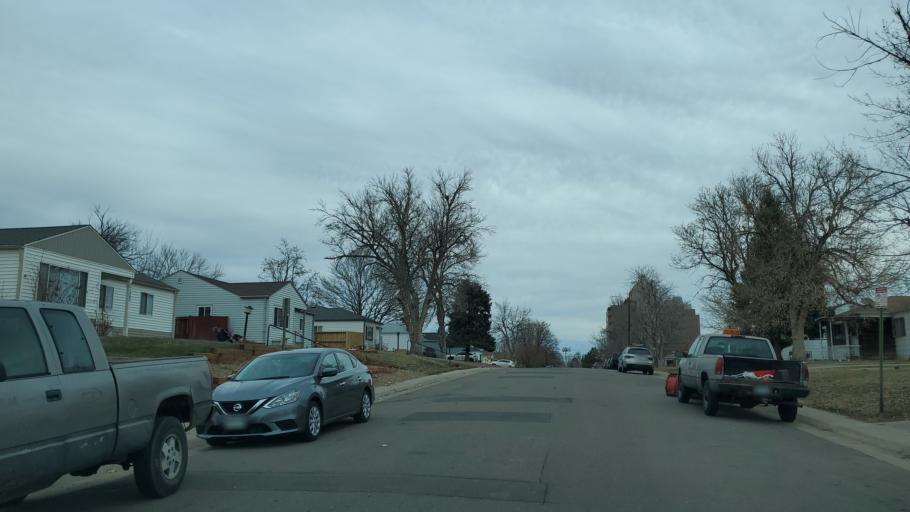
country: US
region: Colorado
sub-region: Arapahoe County
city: Sheridan
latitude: 39.6933
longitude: -105.0087
